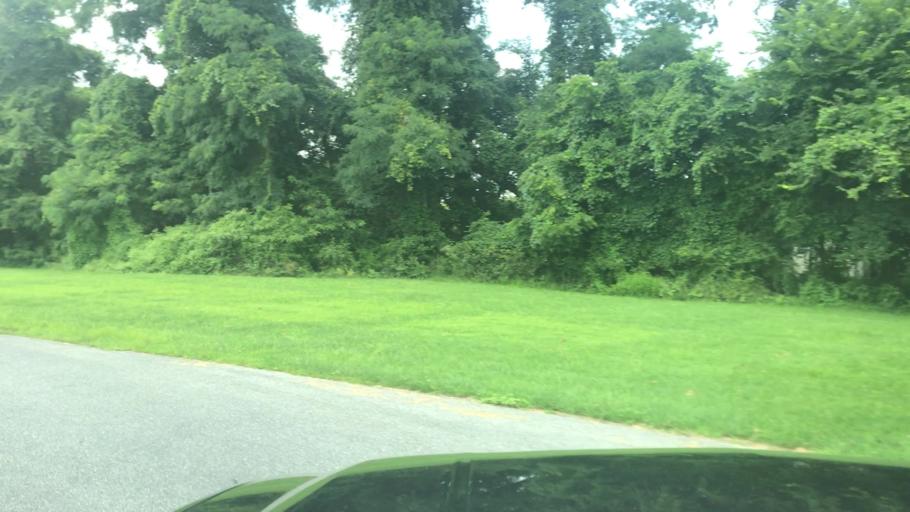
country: US
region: Pennsylvania
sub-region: Dauphin County
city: Harrisburg
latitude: 40.2894
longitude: -76.8775
